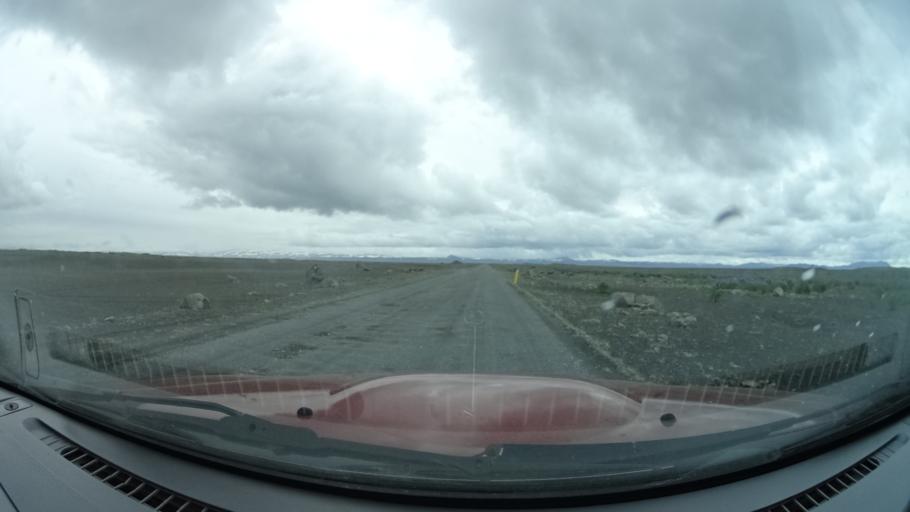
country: IS
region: Northeast
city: Laugar
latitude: 65.6978
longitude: -16.3030
